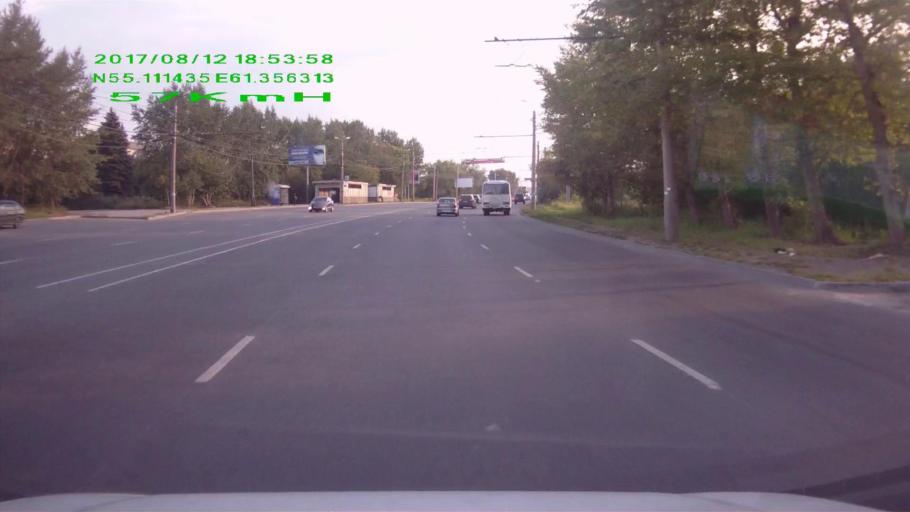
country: RU
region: Chelyabinsk
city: Novosineglazovskiy
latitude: 55.1087
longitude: 61.3524
